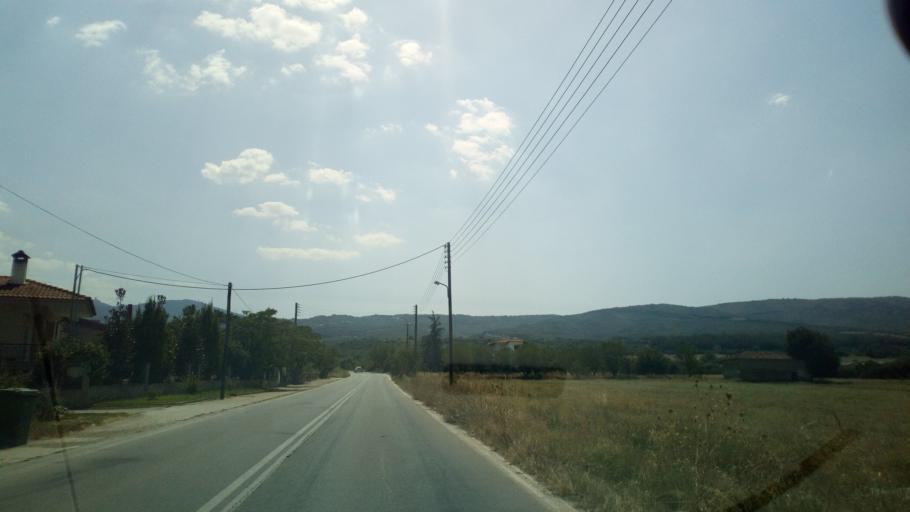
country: GR
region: Central Macedonia
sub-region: Nomos Thessalonikis
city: Agios Vasileios
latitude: 40.6613
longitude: 23.1145
